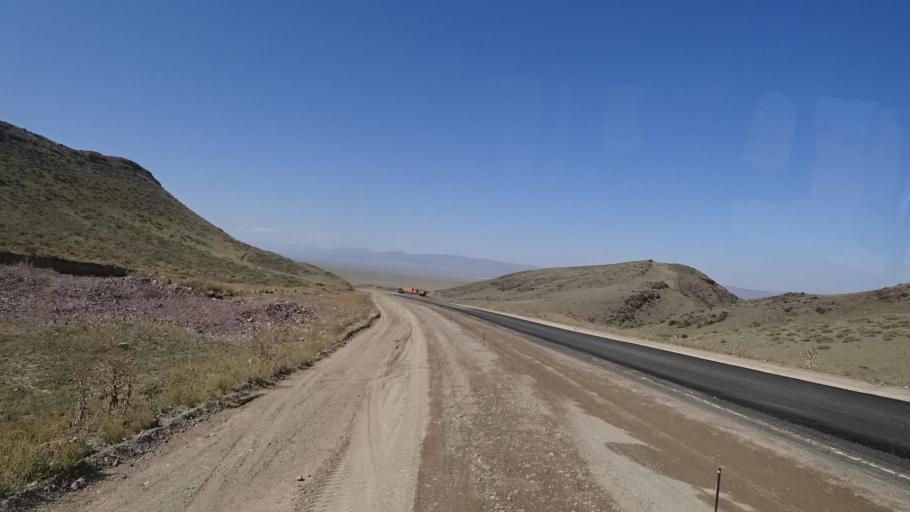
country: KZ
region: Almaty Oblysy
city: Kegen
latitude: 43.1917
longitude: 79.1446
